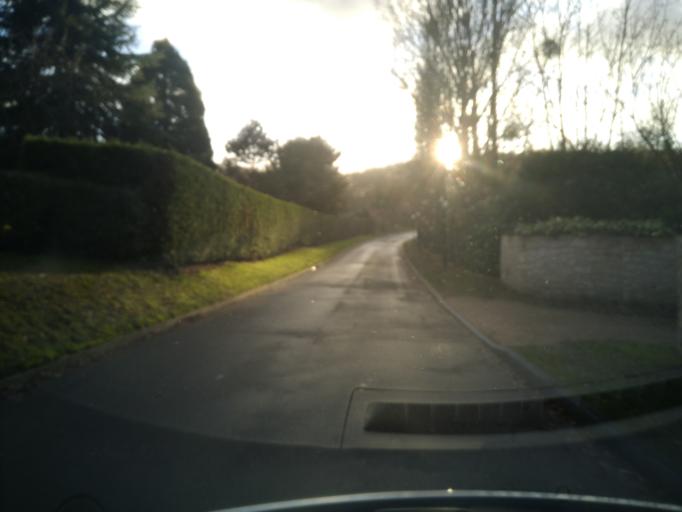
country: FR
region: Ile-de-France
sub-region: Departement des Yvelines
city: Chambourcy
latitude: 48.9018
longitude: 2.0308
